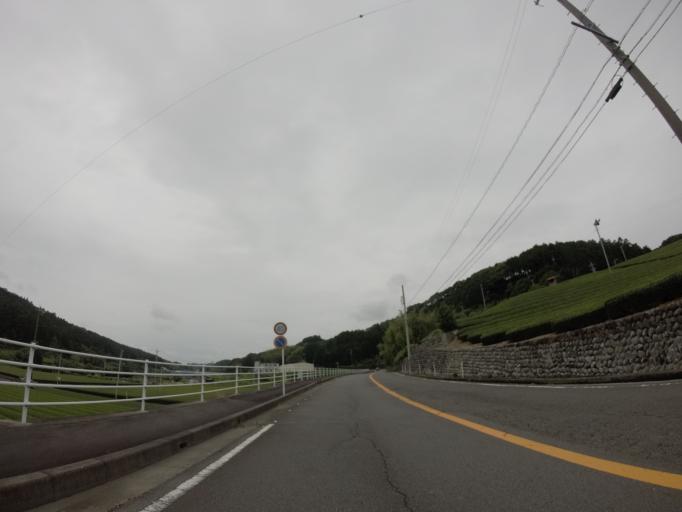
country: JP
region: Shizuoka
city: Shimada
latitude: 34.8071
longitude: 138.1741
